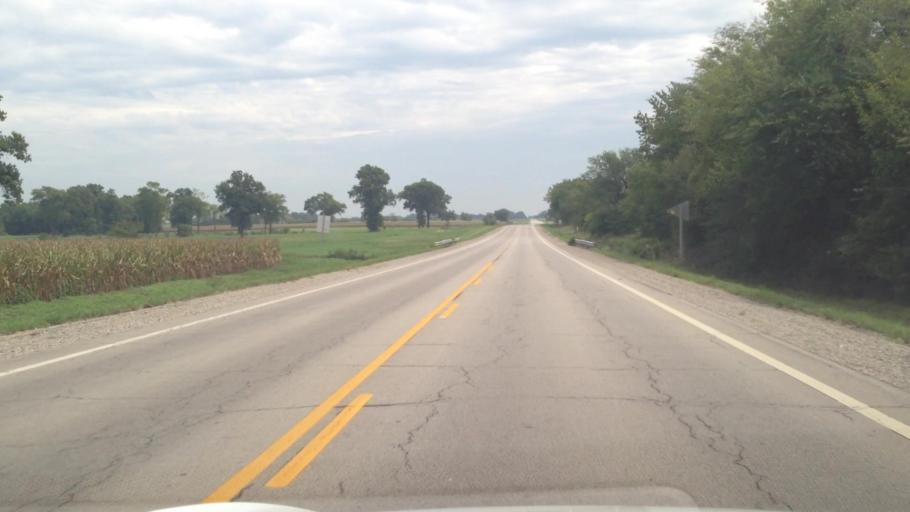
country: US
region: Kansas
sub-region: Crawford County
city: Girard
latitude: 37.5143
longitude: -94.8874
